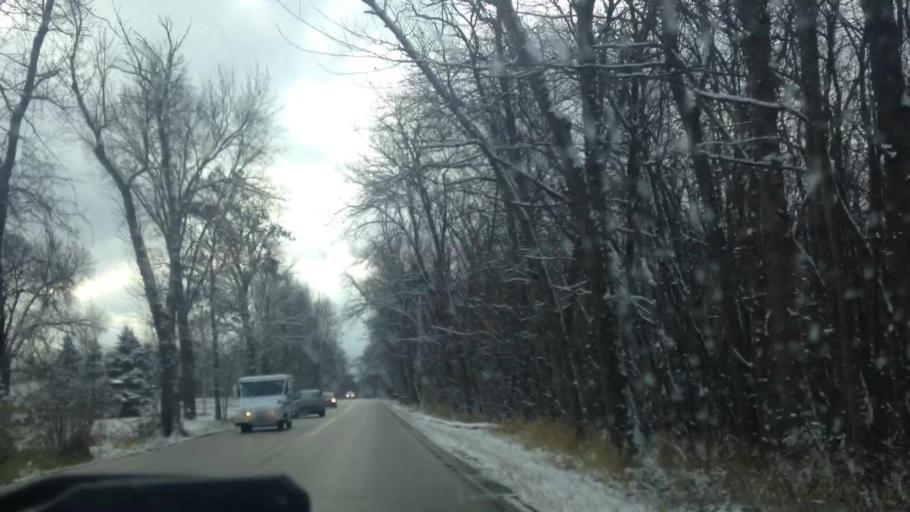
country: US
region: Wisconsin
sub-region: Waukesha County
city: Lannon
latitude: 43.1836
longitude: -88.1826
